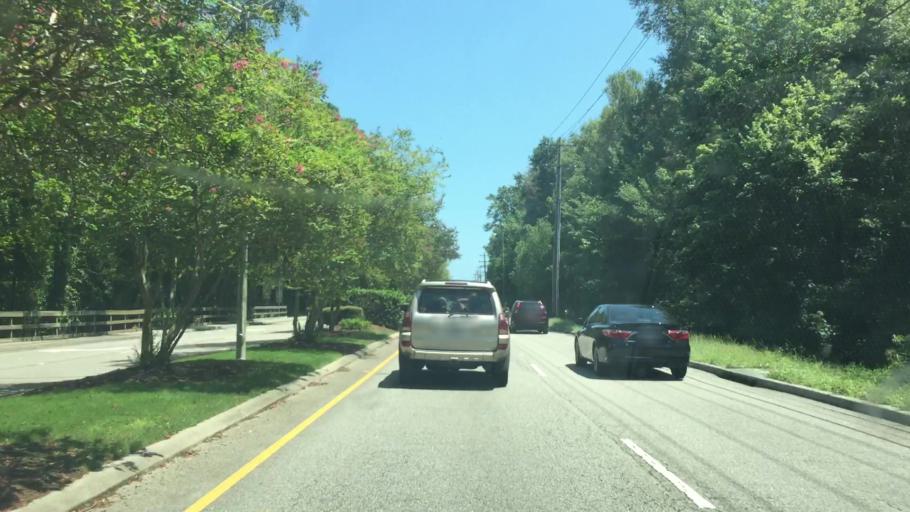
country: US
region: South Carolina
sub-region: Horry County
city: North Myrtle Beach
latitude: 33.8442
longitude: -78.6500
